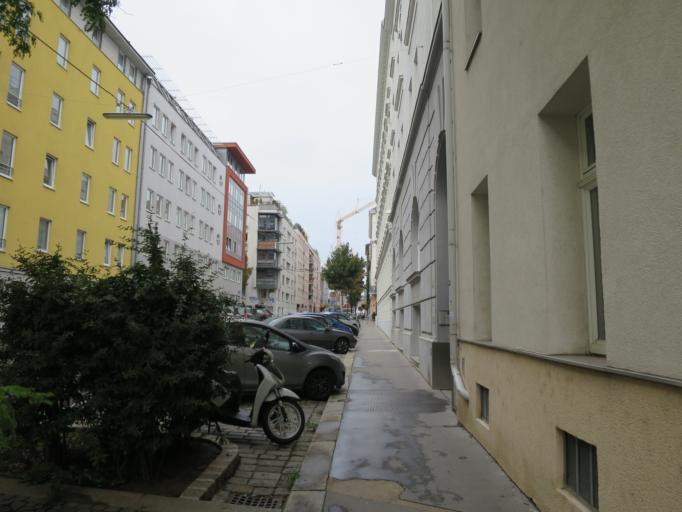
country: AT
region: Vienna
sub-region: Wien Stadt
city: Vienna
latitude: 48.1980
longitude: 16.3344
